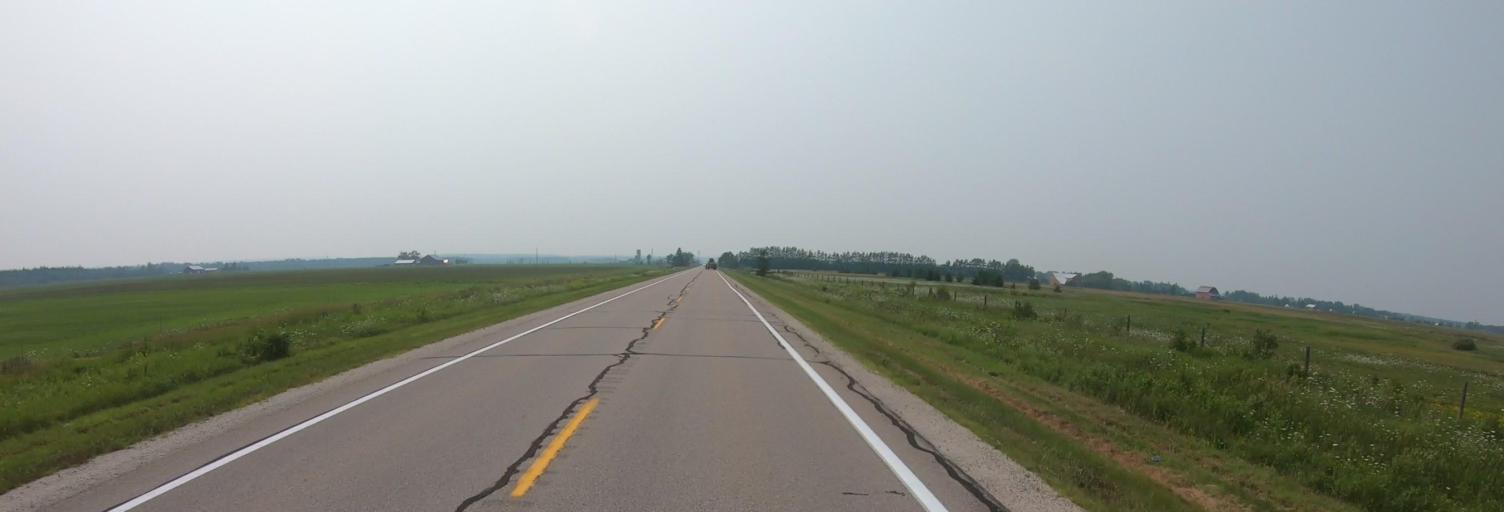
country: US
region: Michigan
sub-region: Chippewa County
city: Sault Ste. Marie
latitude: 46.1292
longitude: -84.3534
